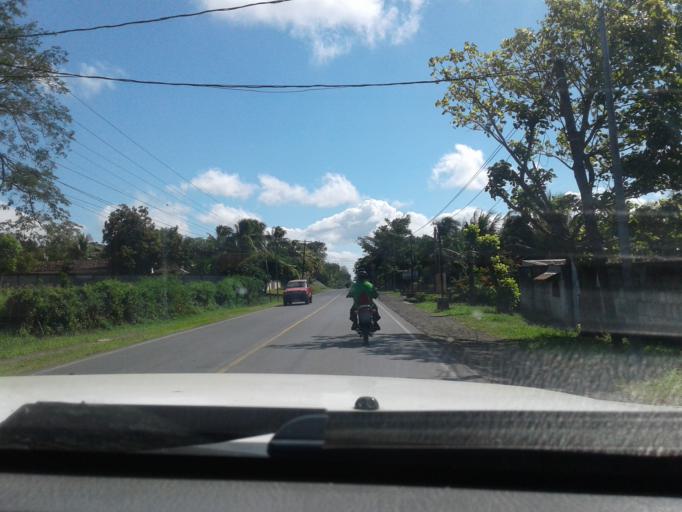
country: NI
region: Carazo
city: Jinotepe
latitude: 11.8267
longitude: -86.1702
